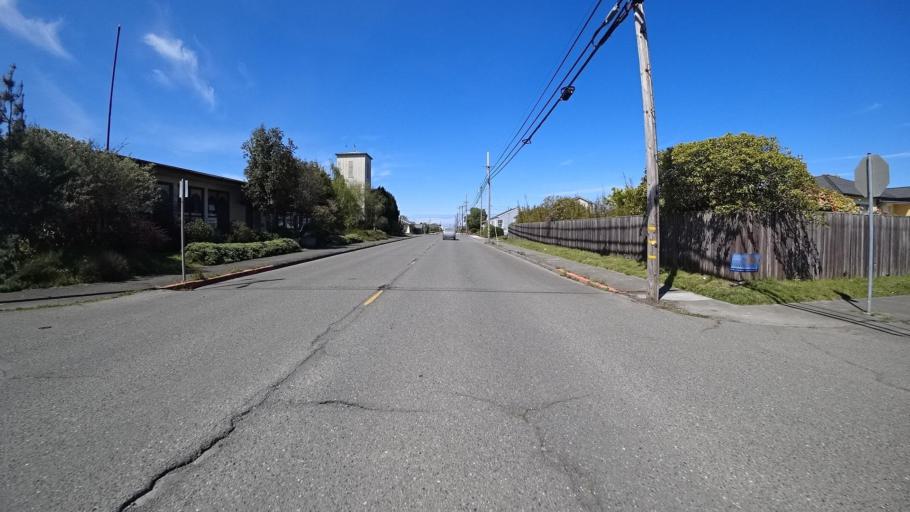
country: US
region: California
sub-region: Humboldt County
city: Cutten
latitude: 40.7828
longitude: -124.1568
